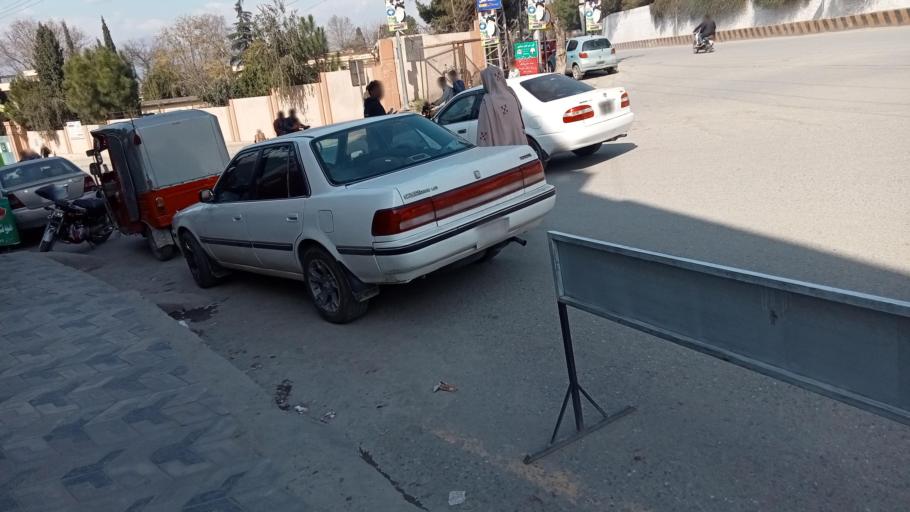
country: PK
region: Khyber Pakhtunkhwa
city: Saidu Sharif
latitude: 34.7525
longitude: 72.3569
